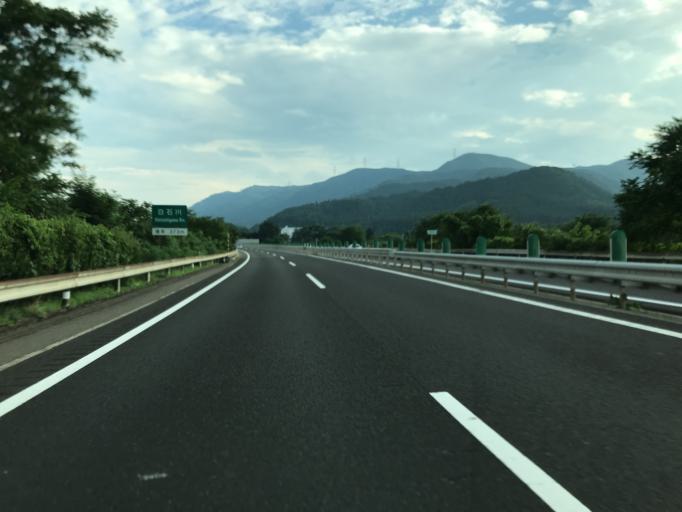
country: JP
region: Miyagi
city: Shiroishi
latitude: 38.0080
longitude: 140.6098
